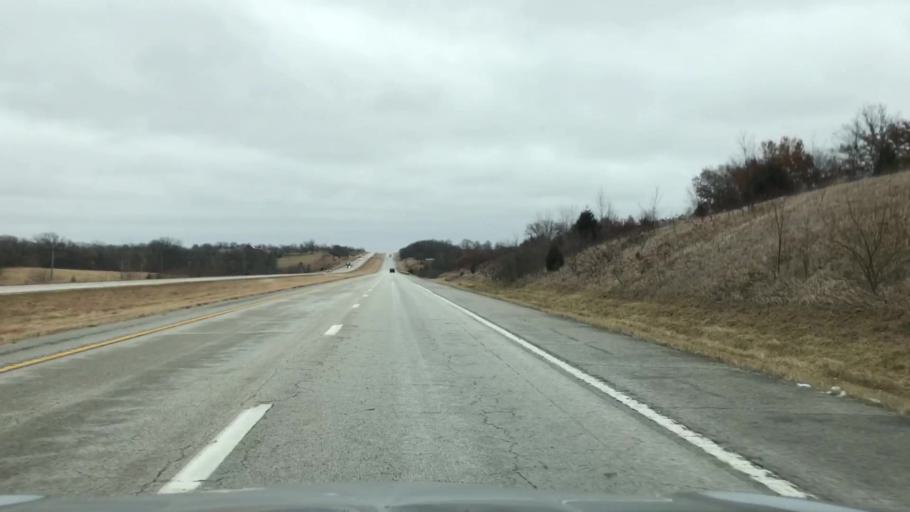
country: US
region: Missouri
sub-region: Clinton County
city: Cameron
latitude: 39.7504
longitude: -94.1239
